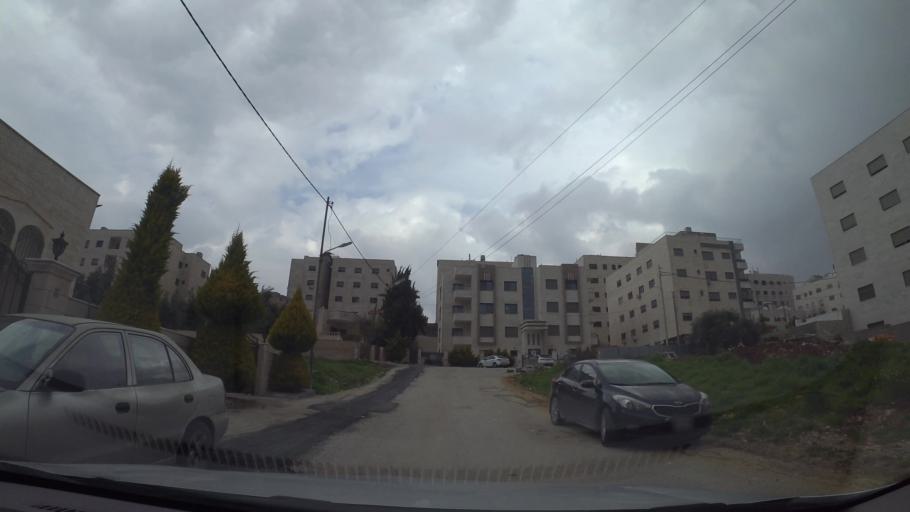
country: JO
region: Amman
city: Umm as Summaq
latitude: 31.8858
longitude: 35.8593
